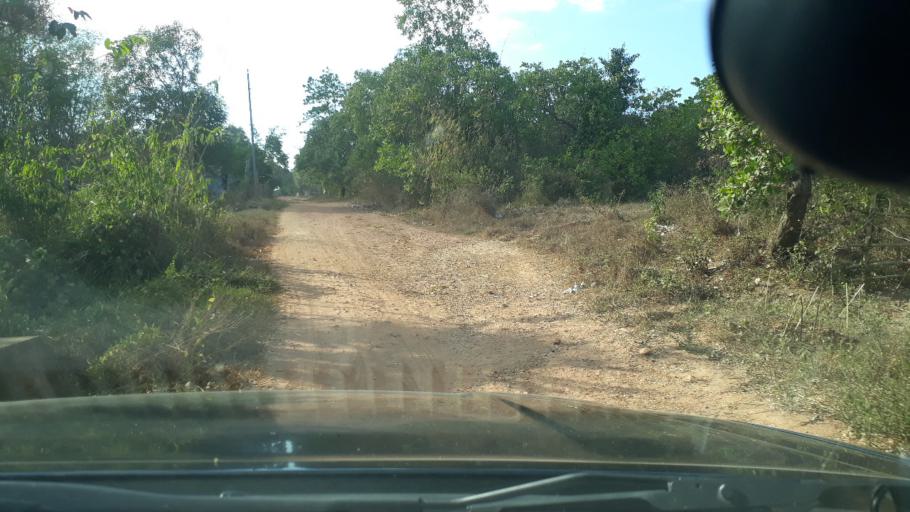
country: PH
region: Mimaropa
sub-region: Province of Palawan
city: Salvacion
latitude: 12.1509
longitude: 120.0921
